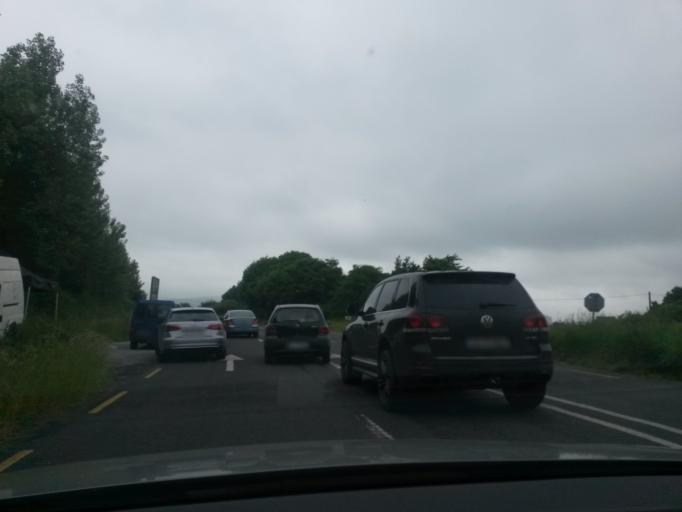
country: IE
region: Munster
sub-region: Ciarrai
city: Ballybunnion
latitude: 52.4787
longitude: -9.6224
